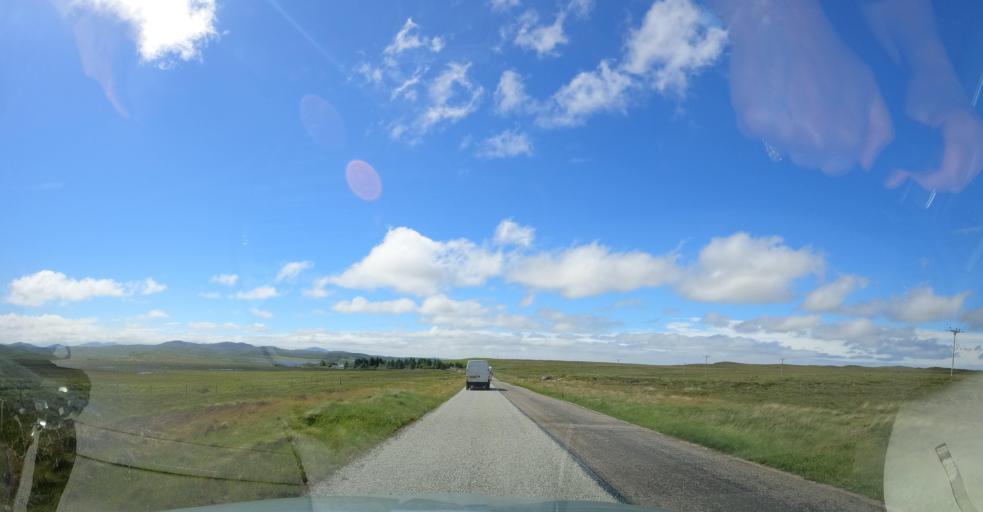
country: GB
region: Scotland
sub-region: Eilean Siar
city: Isle of Lewis
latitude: 58.1871
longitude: -6.6889
